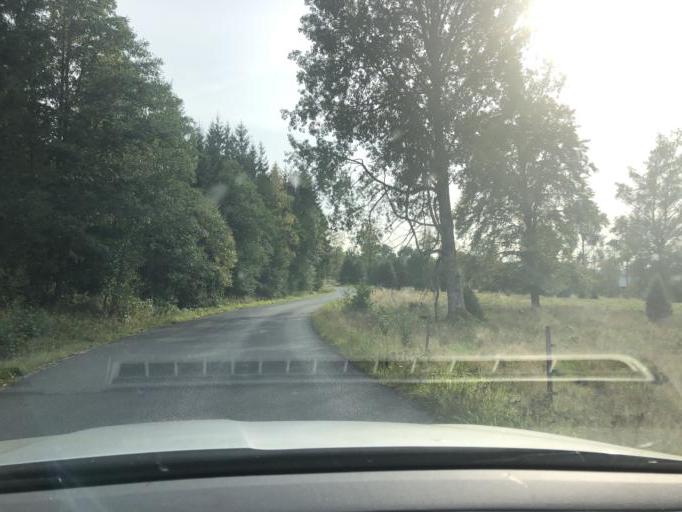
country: SE
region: Joenkoeping
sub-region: Vetlanda Kommun
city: Ekenassjon
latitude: 57.4894
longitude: 14.8927
